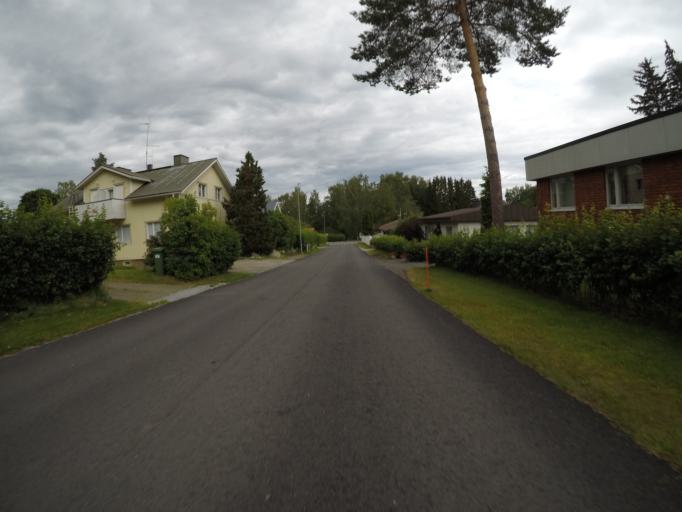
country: FI
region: Haeme
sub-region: Haemeenlinna
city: Haemeenlinna
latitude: 60.9838
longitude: 24.4611
